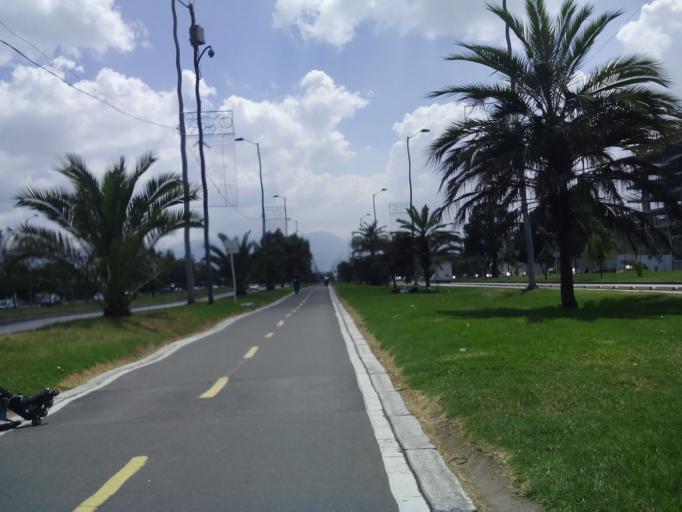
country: CO
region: Bogota D.C.
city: Bogota
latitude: 4.6775
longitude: -74.1187
